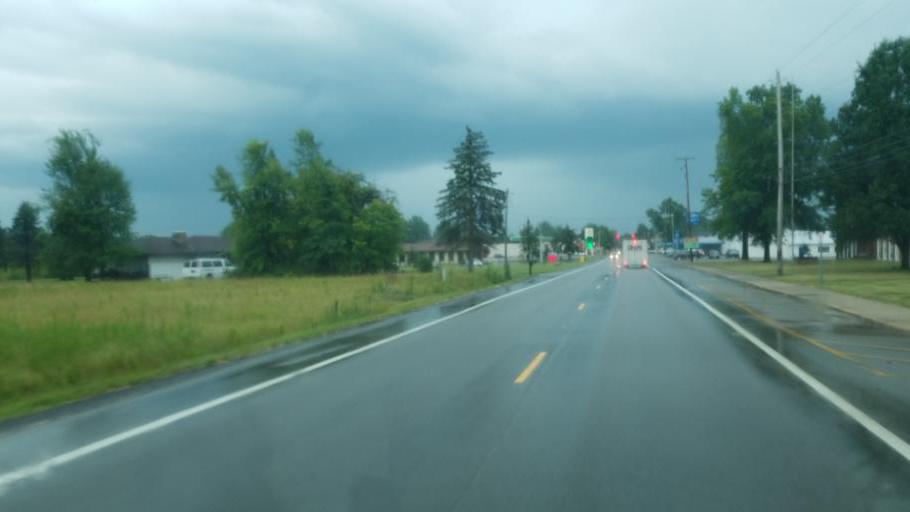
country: US
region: Ohio
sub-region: Trumbull County
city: Champion Heights
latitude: 41.3108
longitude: -80.8503
